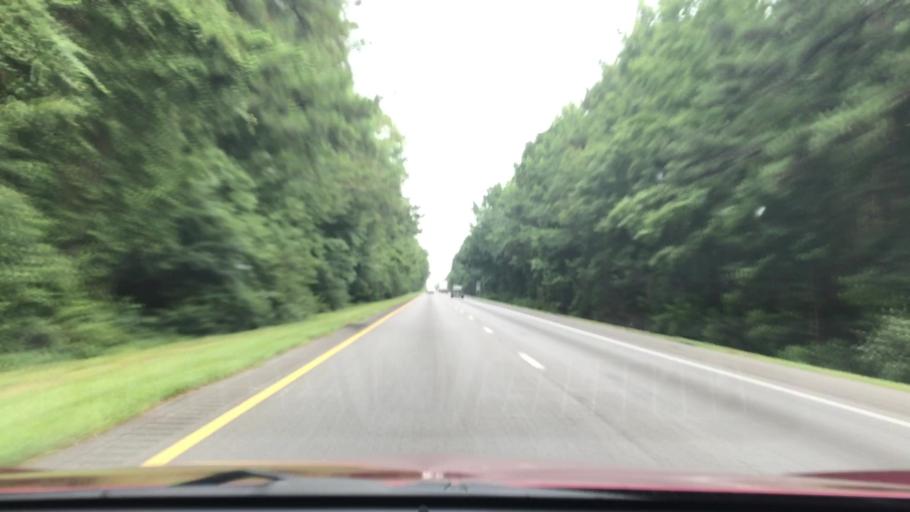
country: US
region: South Carolina
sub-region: Dorchester County
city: Ridgeville
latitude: 33.1409
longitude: -80.3176
